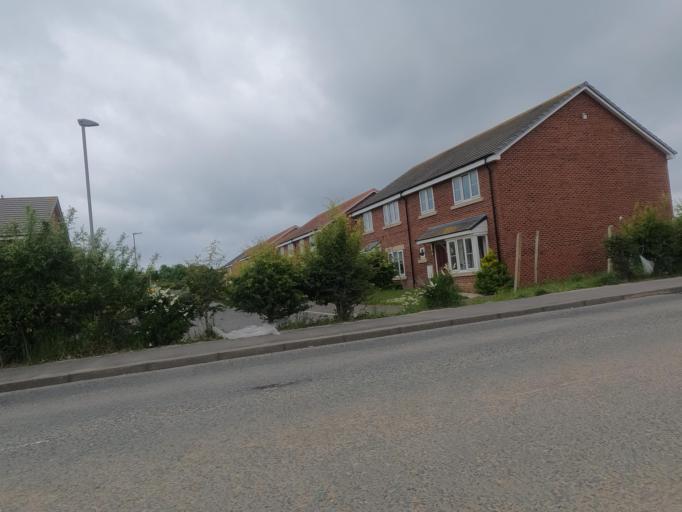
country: GB
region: England
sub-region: Northumberland
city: Blyth
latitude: 55.1059
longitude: -1.5287
